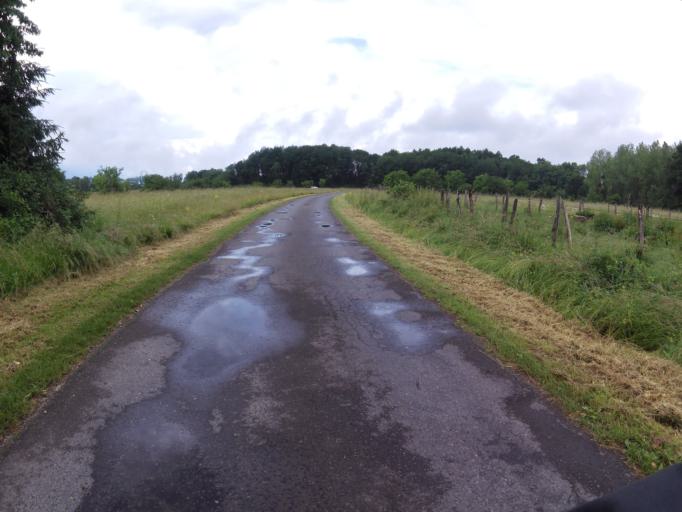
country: FR
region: Champagne-Ardenne
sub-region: Departement de la Marne
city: Sermaize-les-Bains
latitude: 48.7734
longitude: 4.9261
